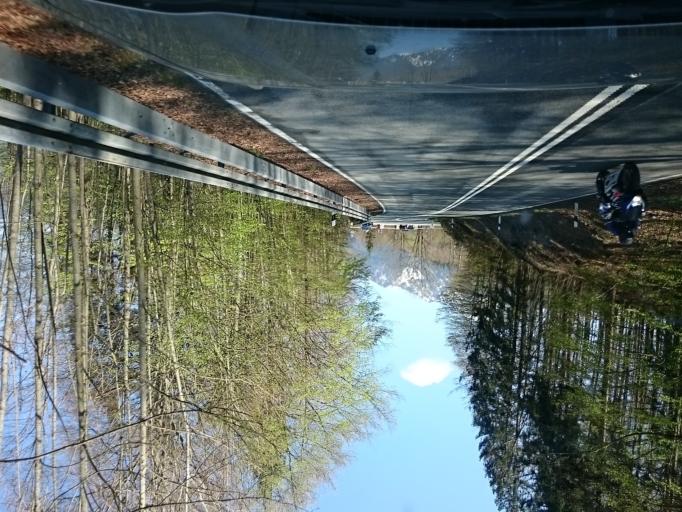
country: DE
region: Bavaria
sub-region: Upper Bavaria
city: Kochel
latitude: 47.6329
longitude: 11.3549
